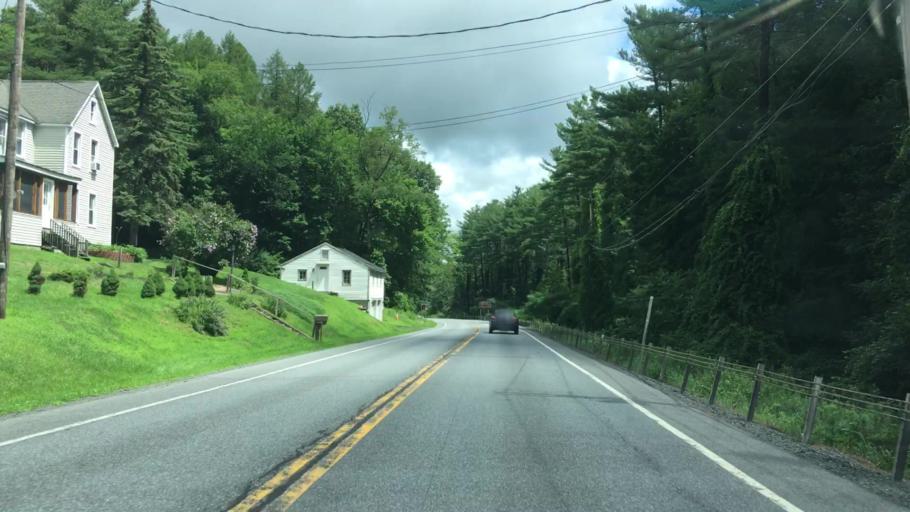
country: US
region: New York
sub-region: Rensselaer County
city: Poestenkill
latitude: 42.8174
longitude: -73.5281
